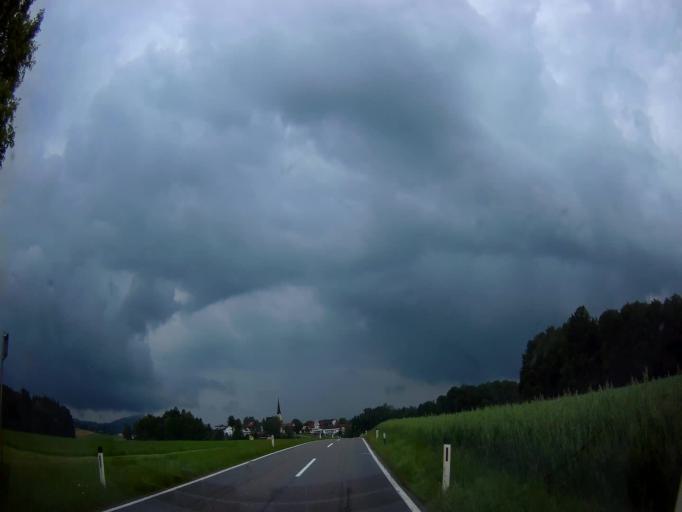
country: AT
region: Salzburg
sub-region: Politischer Bezirk Salzburg-Umgebung
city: Mattsee
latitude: 48.0197
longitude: 13.1310
